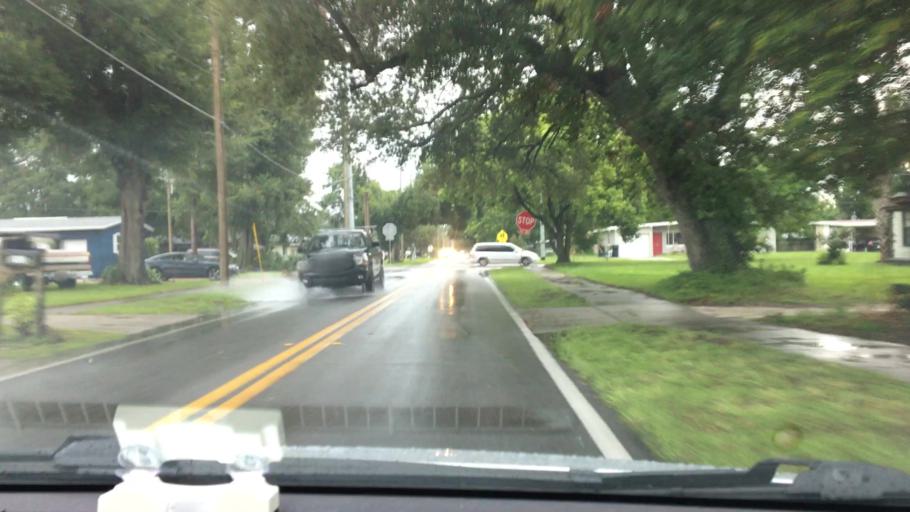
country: US
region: Florida
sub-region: Orange County
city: Conway
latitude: 28.5067
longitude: -81.3392
